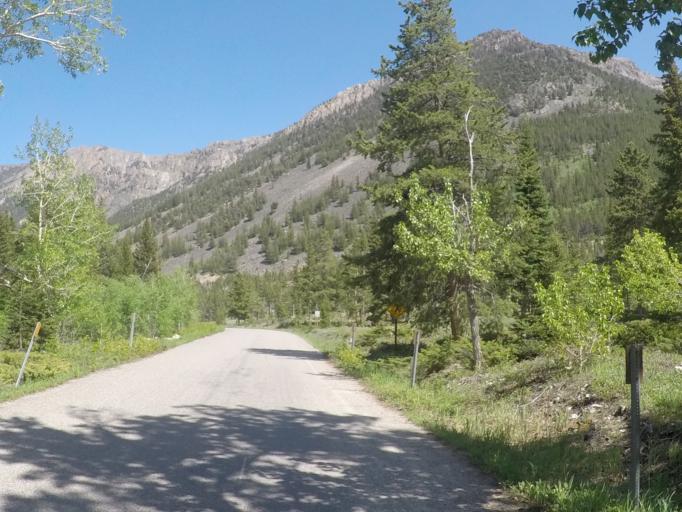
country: US
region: Montana
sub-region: Carbon County
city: Red Lodge
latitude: 45.0585
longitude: -109.4090
